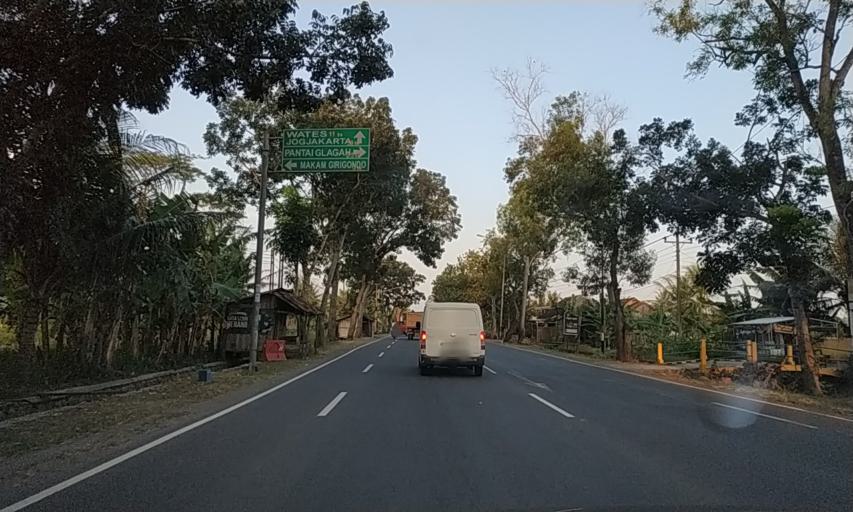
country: ID
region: Daerah Istimewa Yogyakarta
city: Srandakan
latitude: -7.8878
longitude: 110.0908
